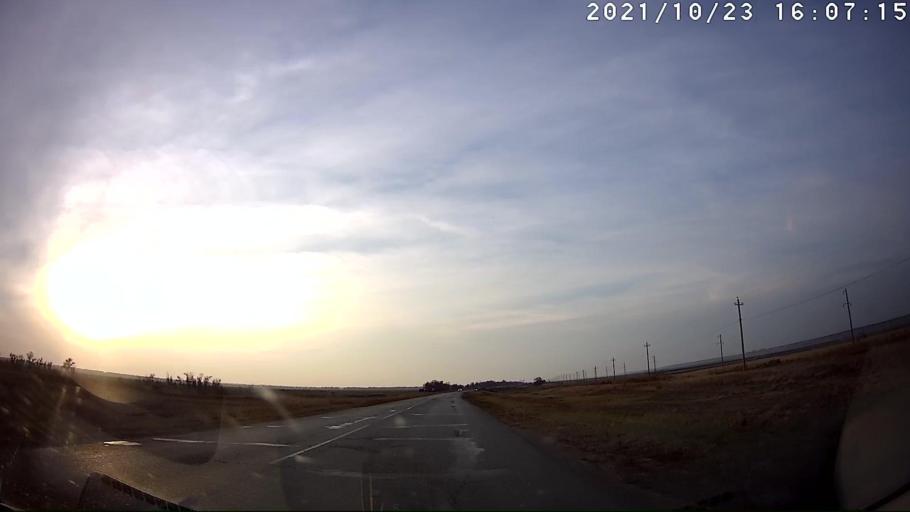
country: RU
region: Volgograd
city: Kotel'nikovo
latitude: 47.9323
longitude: 43.7405
